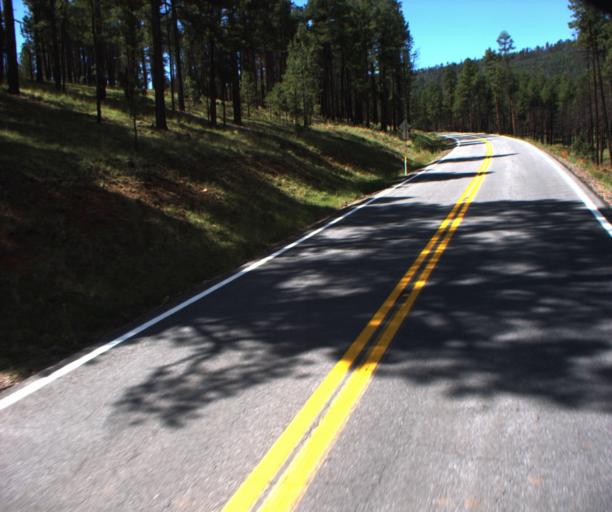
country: US
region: Arizona
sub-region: Apache County
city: Eagar
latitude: 33.7426
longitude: -109.2055
